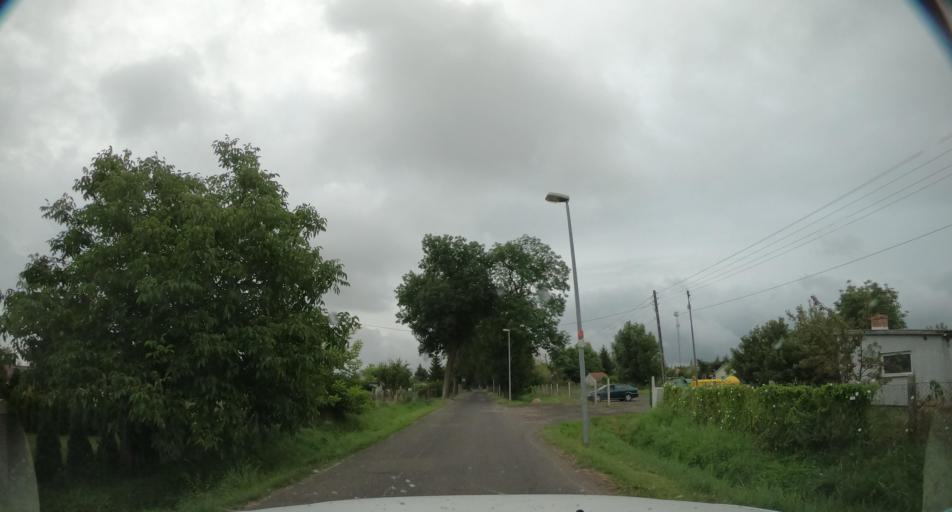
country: PL
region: West Pomeranian Voivodeship
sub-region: Powiat stargardzki
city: Stargard Szczecinski
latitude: 53.3369
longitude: 15.0591
